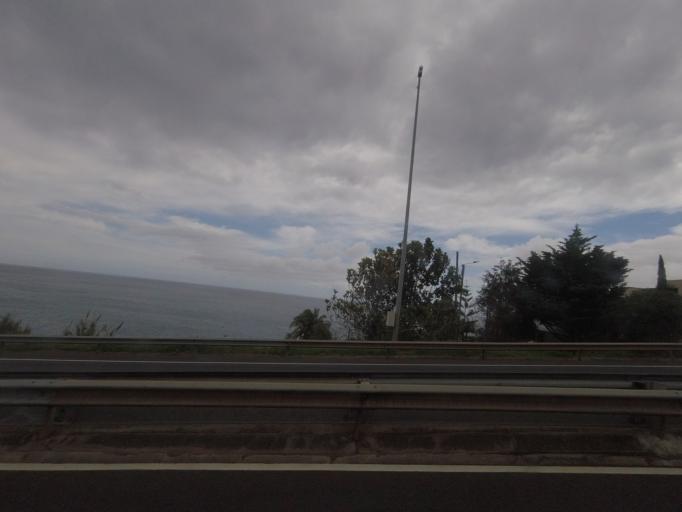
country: PT
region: Madeira
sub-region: Santa Cruz
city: Santa Cruz
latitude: 32.6798
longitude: -16.7985
